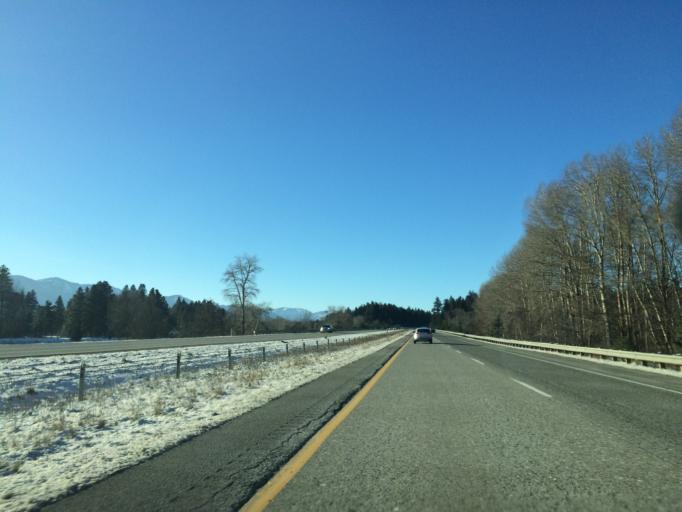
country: US
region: Washington
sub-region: Kittitas County
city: Cle Elum
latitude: 47.1921
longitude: -120.9420
